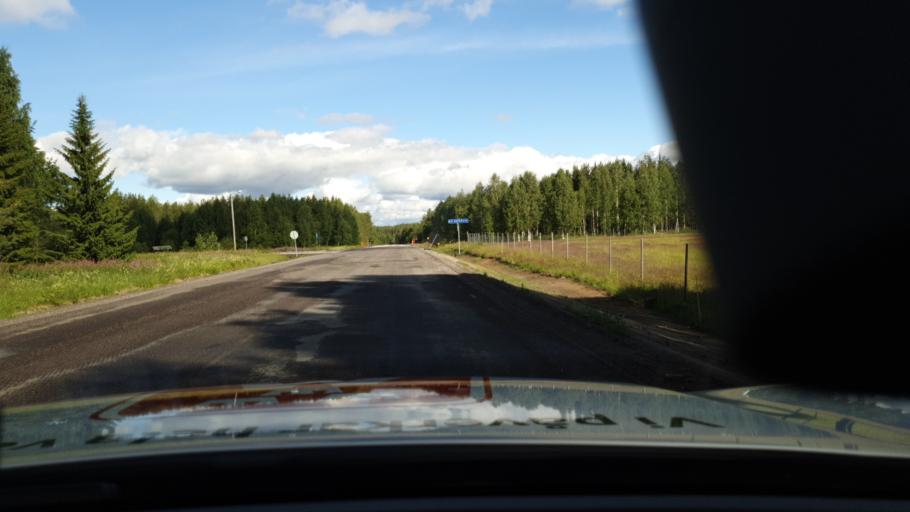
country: SE
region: Norrbotten
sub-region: Bodens Kommun
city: Boden
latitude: 65.8883
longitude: 21.3911
